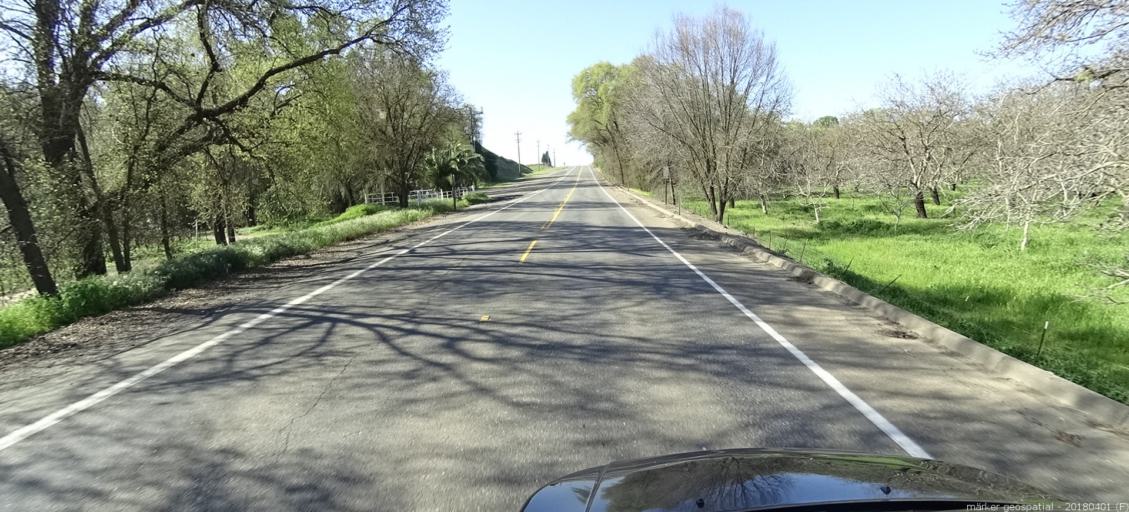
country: US
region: California
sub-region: Sacramento County
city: Rancho Murieta
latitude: 38.4885
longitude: -121.1626
